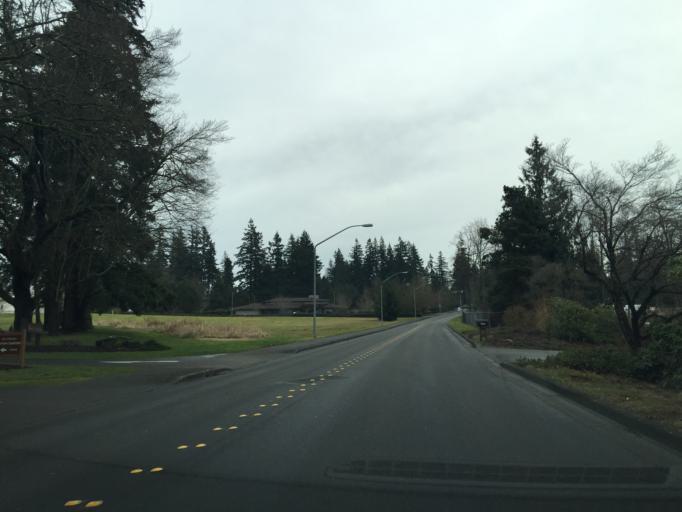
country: US
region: Washington
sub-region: Whatcom County
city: Geneva
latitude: 48.7475
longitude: -122.4444
